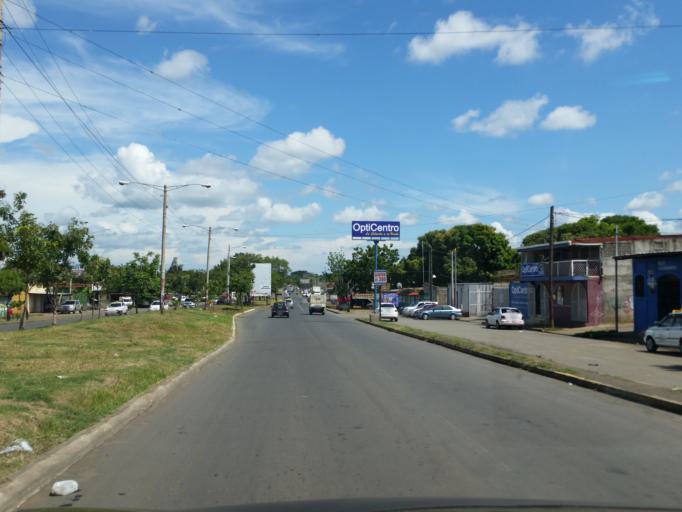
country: NI
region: Managua
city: Managua
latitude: 12.1383
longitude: -86.2042
